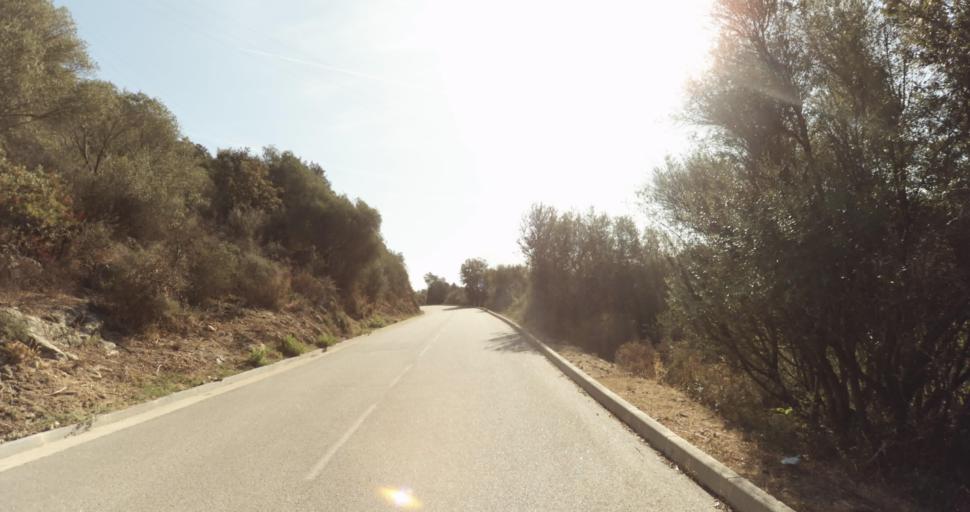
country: FR
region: Corsica
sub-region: Departement de la Corse-du-Sud
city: Ajaccio
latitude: 41.9327
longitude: 8.7039
